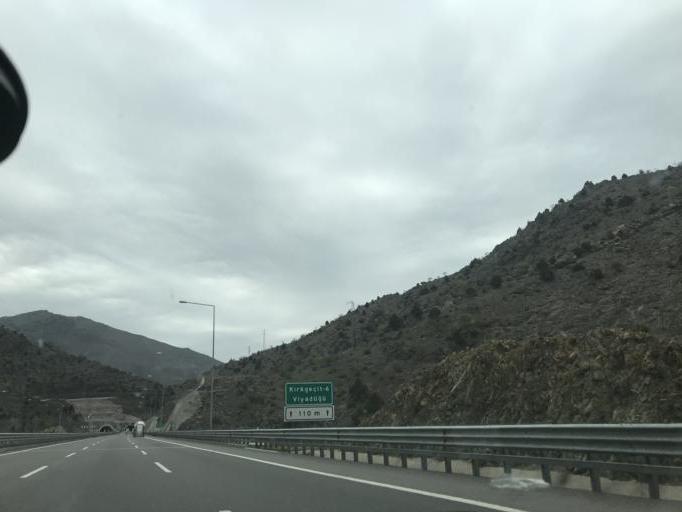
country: TR
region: Nigde
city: Ciftehan
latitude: 37.5538
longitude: 34.7731
